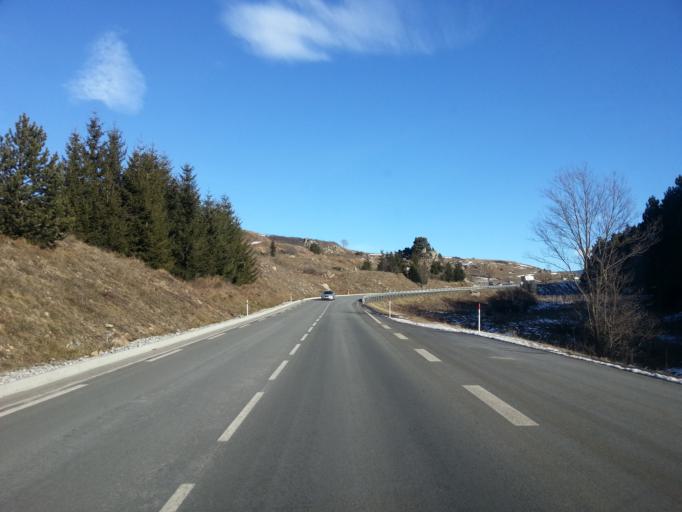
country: ES
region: Catalonia
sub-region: Provincia de Girona
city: Llivia
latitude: 42.4881
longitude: 2.0675
